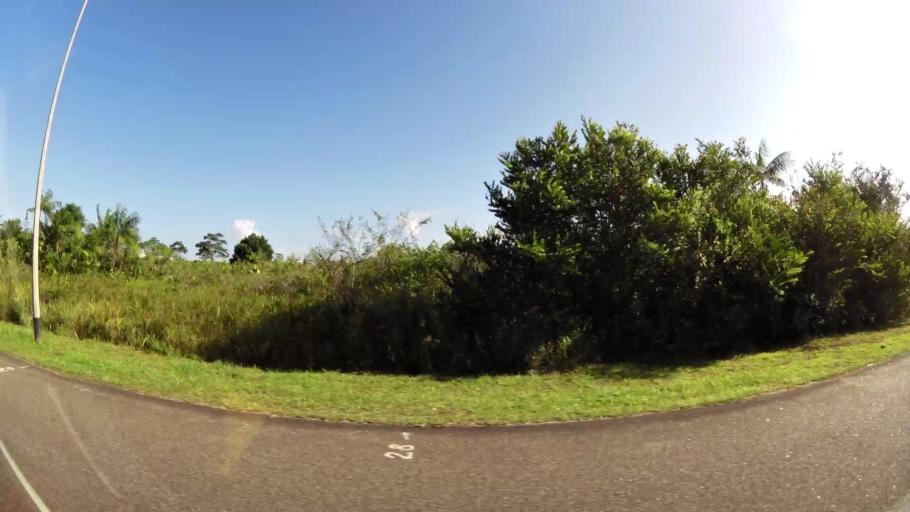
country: GF
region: Guyane
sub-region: Guyane
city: Matoury
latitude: 4.8601
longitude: -52.2742
